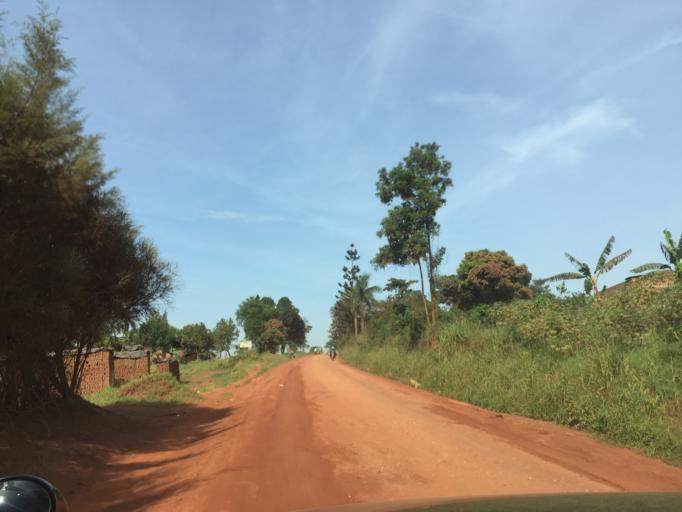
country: UG
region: Central Region
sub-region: Wakiso District
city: Wakiso
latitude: 0.4631
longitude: 32.5517
